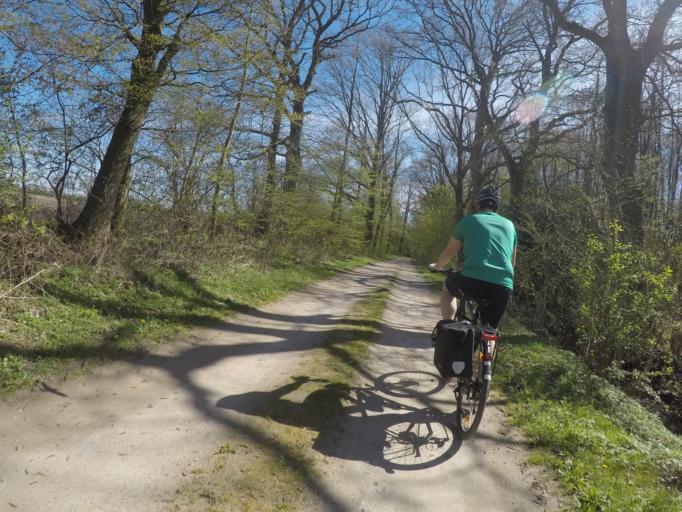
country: DE
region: Schleswig-Holstein
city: Bargfeld-Stegen
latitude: 53.7353
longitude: 10.1777
